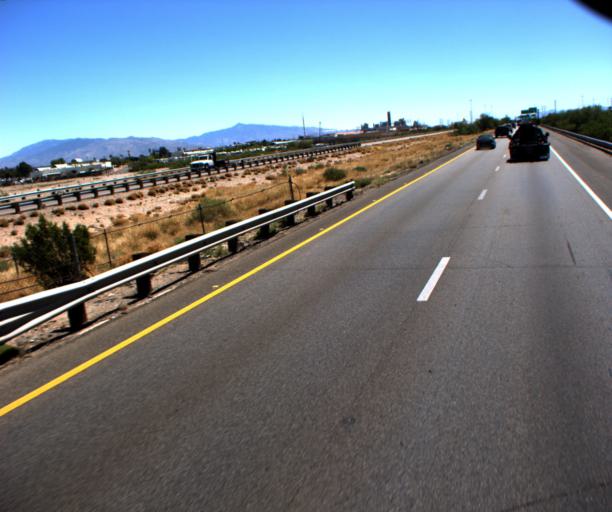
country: US
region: Arizona
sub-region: Pima County
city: South Tucson
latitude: 32.1668
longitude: -110.9262
